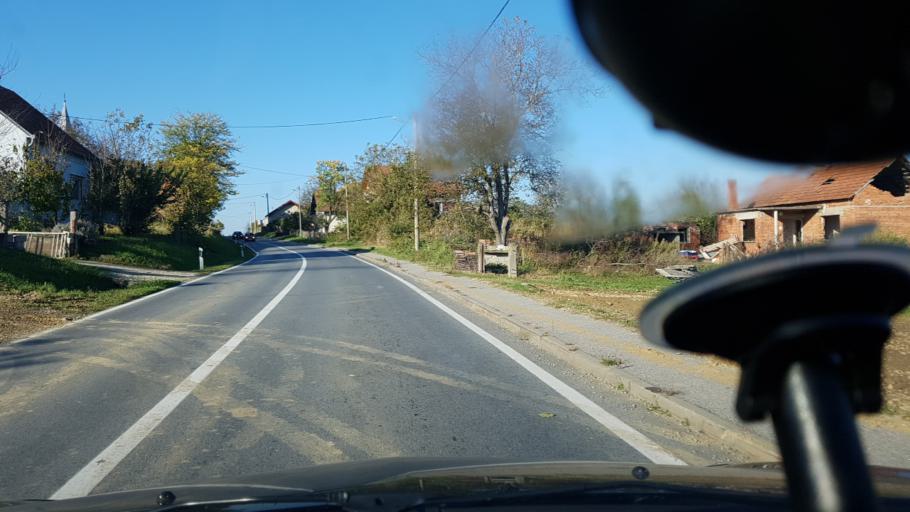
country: HR
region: Bjelovarsko-Bilogorska
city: Bjelovar
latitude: 45.9487
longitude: 16.8910
